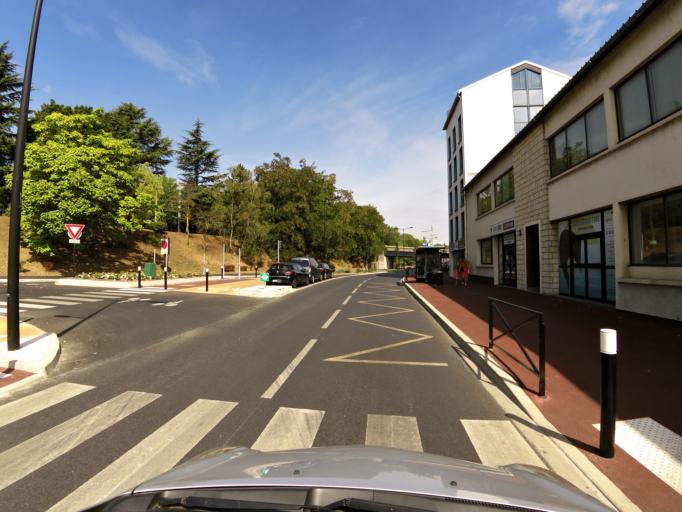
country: FR
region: Ile-de-France
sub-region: Departement du Val-de-Marne
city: Joinville-le-Pont
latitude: 48.8228
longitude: 2.4657
